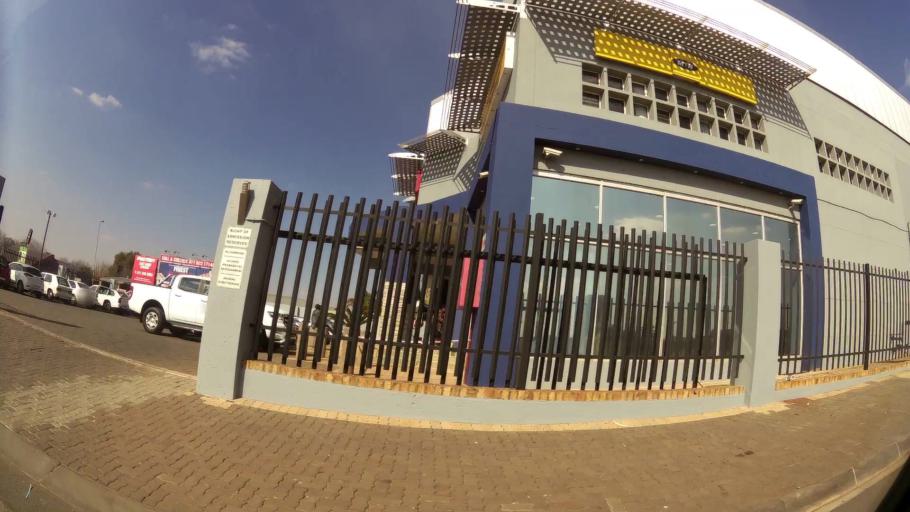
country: ZA
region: Gauteng
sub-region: Ekurhuleni Metropolitan Municipality
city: Boksburg
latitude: -26.1864
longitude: 28.2380
